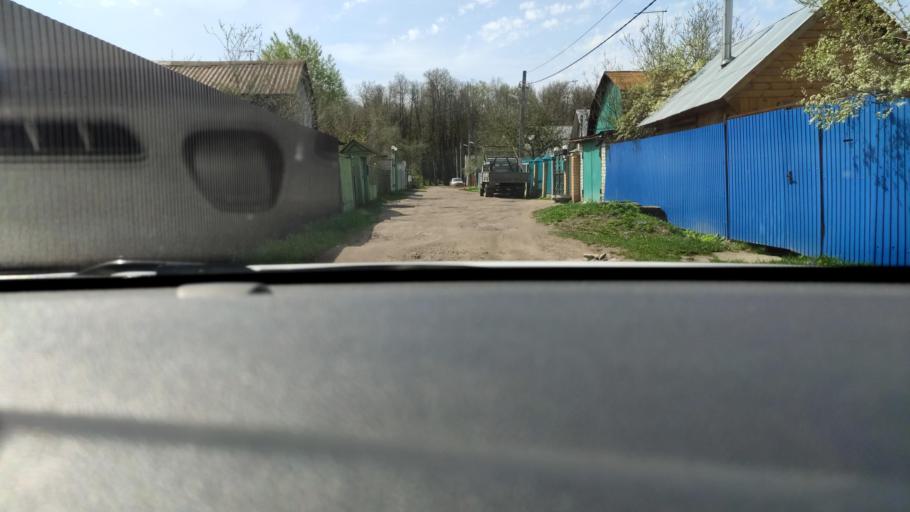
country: RU
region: Tatarstan
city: Osinovo
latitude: 55.8491
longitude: 48.8848
